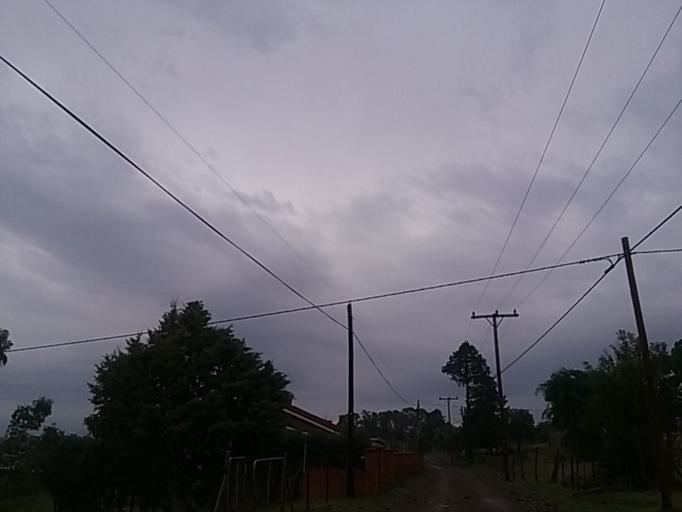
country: LS
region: Berea
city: Teyateyaneng
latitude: -29.1389
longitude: 27.7377
